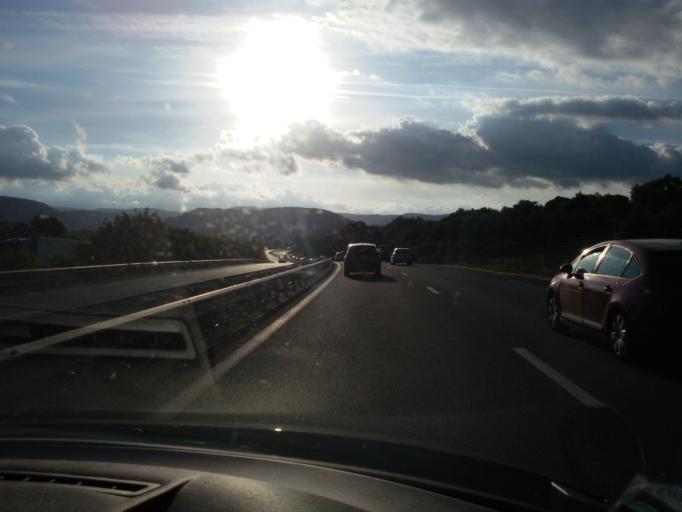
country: FR
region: Languedoc-Roussillon
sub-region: Departement de l'Herault
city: Lodeve
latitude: 43.6851
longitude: 3.3661
